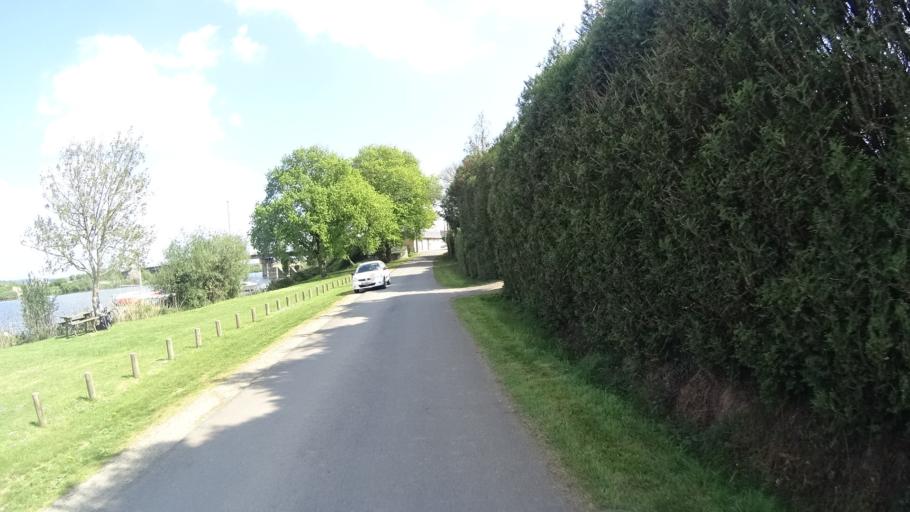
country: FR
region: Brittany
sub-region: Departement du Morbihan
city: Rieux
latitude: 47.5806
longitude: -2.1282
